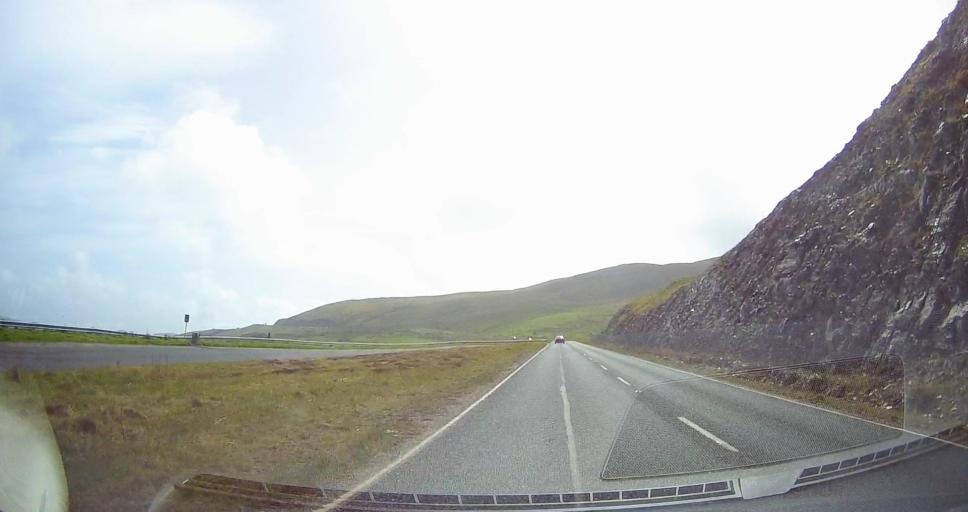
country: GB
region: Scotland
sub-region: Shetland Islands
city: Sandwick
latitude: 60.0308
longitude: -1.2345
